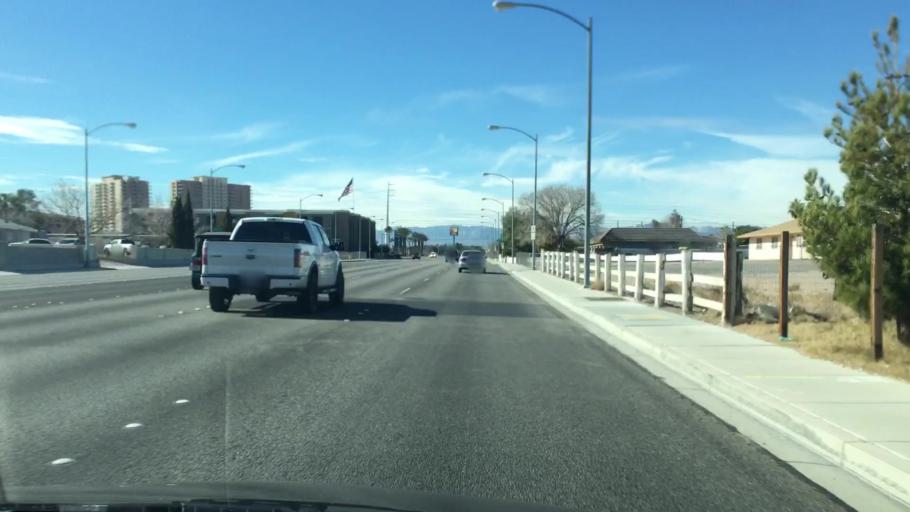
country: US
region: Nevada
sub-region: Clark County
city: Paradise
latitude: 36.0424
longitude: -115.1668
